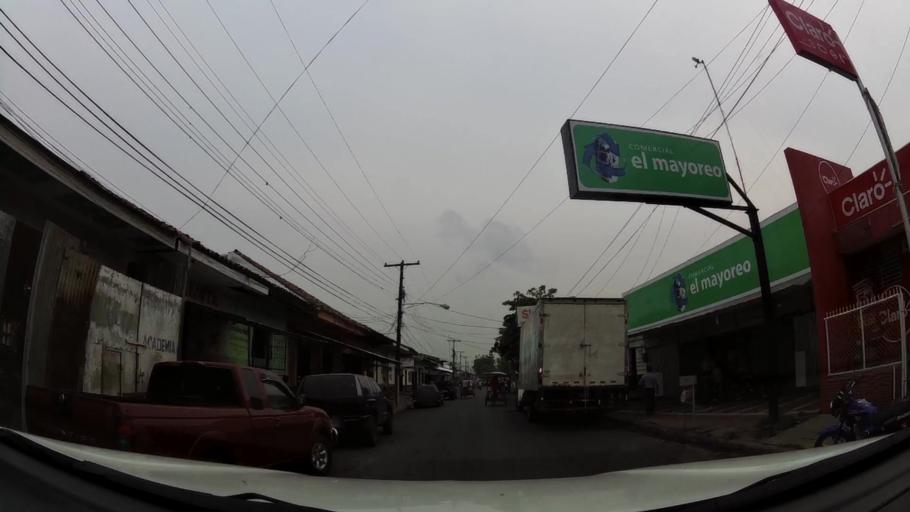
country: NI
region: Leon
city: Leon
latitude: 12.4413
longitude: -86.8739
